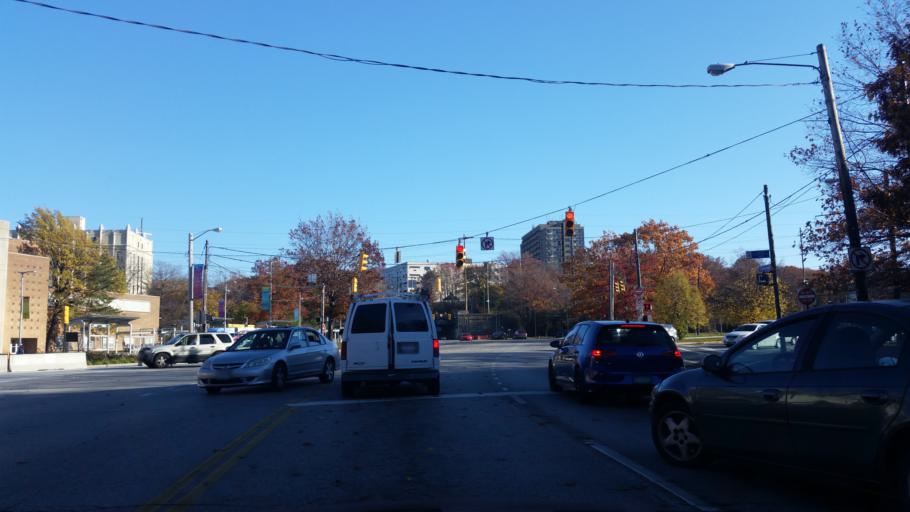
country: US
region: Ohio
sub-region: Cuyahoga County
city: East Cleveland
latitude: 41.5007
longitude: -81.6082
